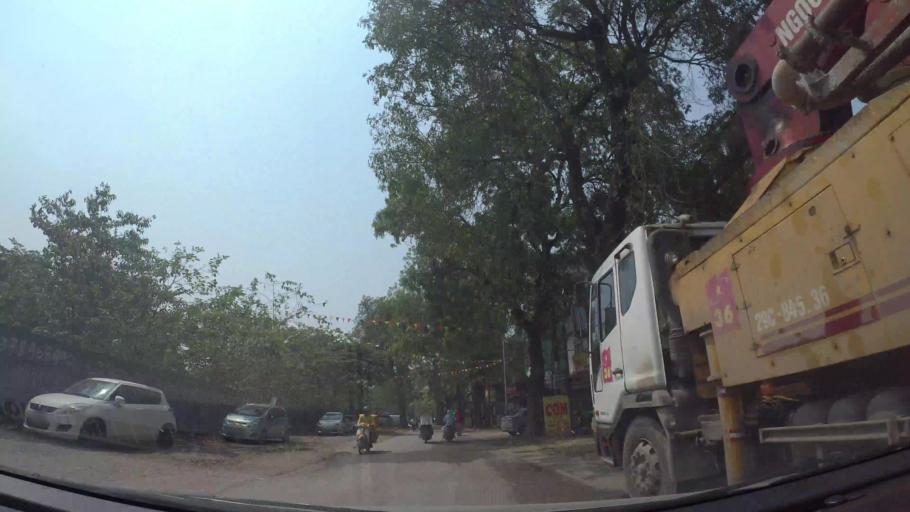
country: VN
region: Ha Noi
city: Ha Dong
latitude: 20.9908
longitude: 105.7636
